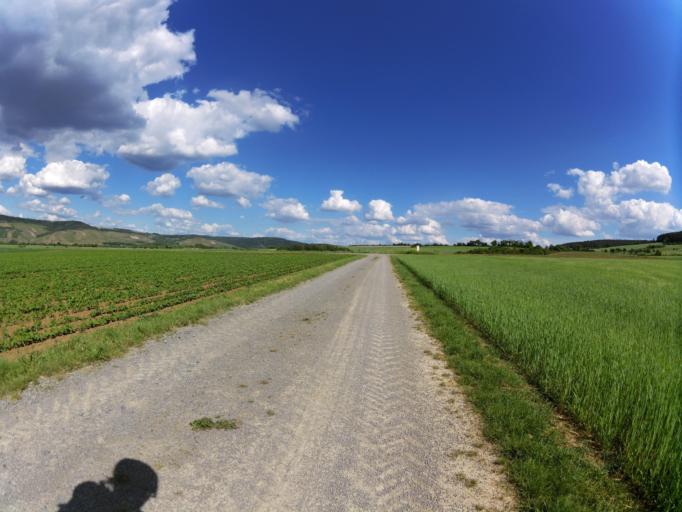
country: DE
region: Bavaria
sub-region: Regierungsbezirk Unterfranken
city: Zellingen
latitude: 49.8776
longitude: 9.8150
